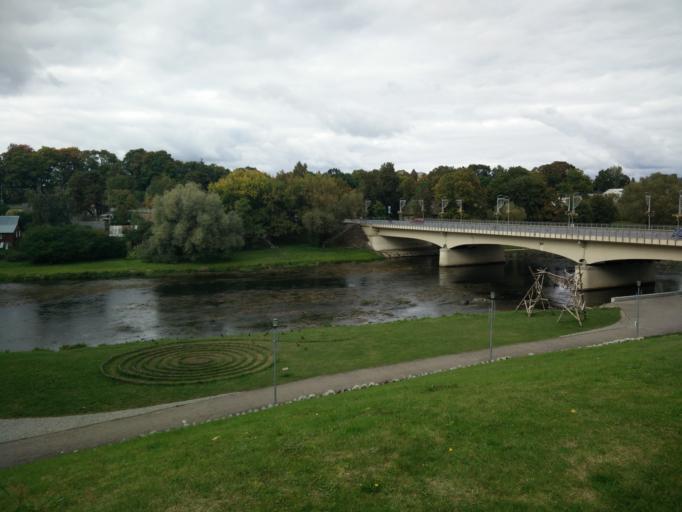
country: LT
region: Utenos apskritis
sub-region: Anyksciai
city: Anyksciai
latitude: 55.5251
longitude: 25.1015
